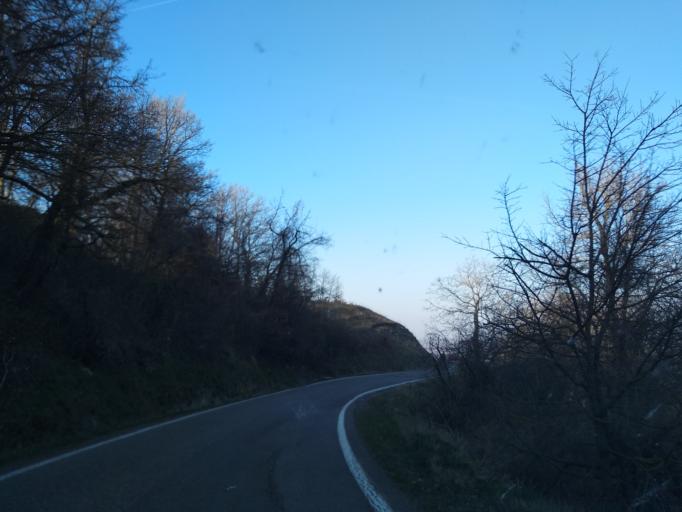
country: IT
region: Emilia-Romagna
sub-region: Provincia di Reggio Emilia
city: Ramiseto
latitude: 44.4115
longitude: 10.2699
